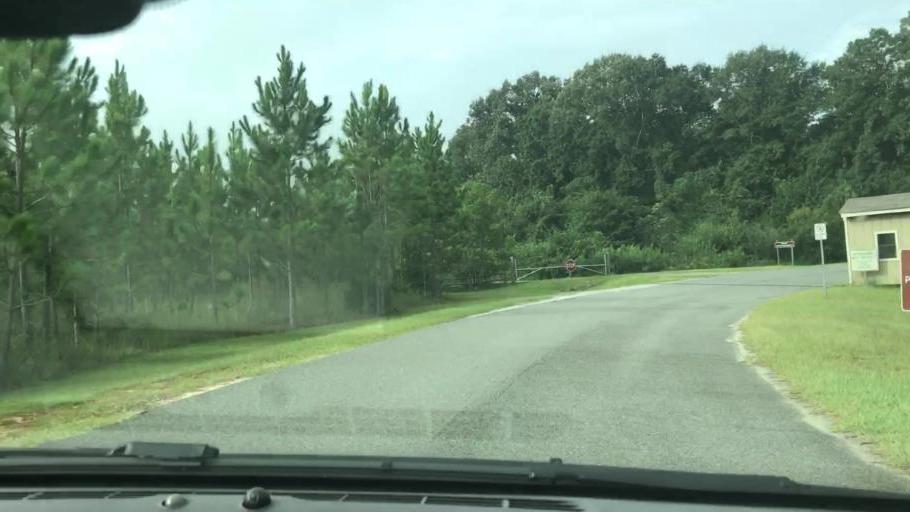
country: US
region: Georgia
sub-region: Stewart County
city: Lumpkin
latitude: 32.0673
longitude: -84.9039
